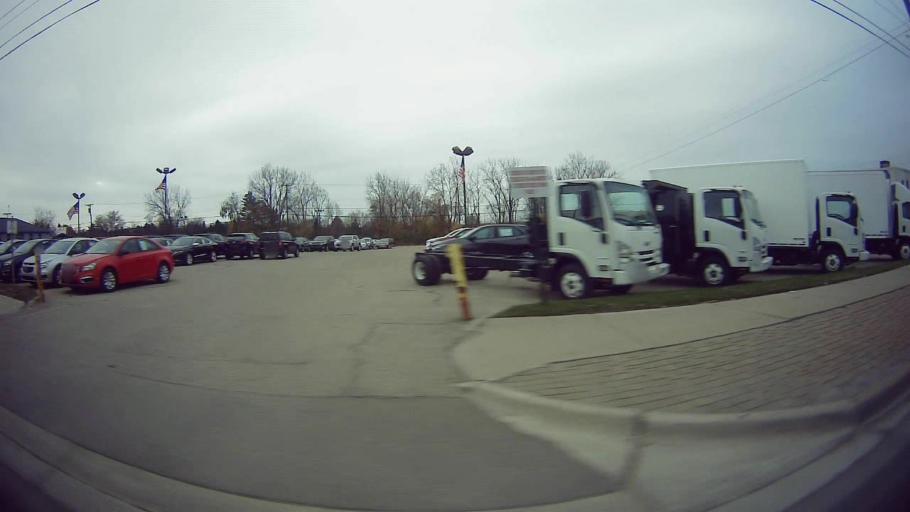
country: US
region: Michigan
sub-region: Oakland County
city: Clarkston
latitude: 42.7203
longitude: -83.4185
